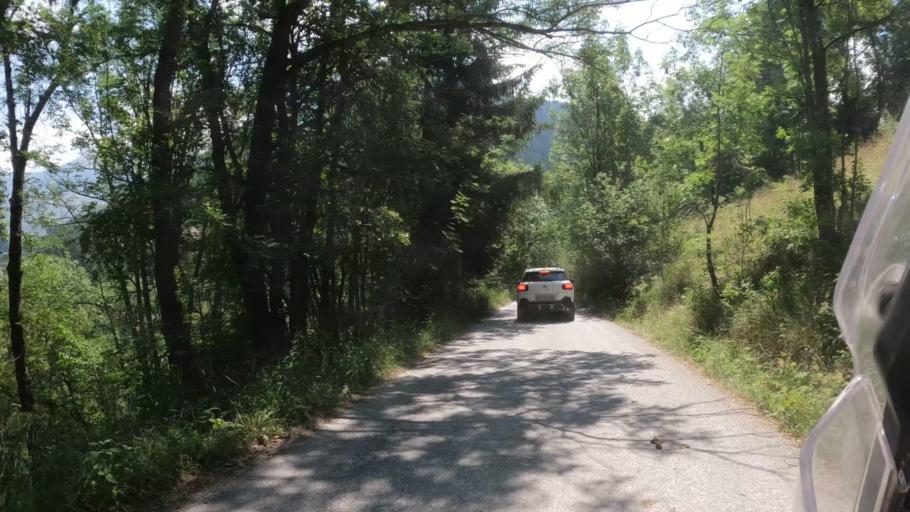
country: IT
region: Piedmont
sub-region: Provincia di Torino
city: Cesana Torinese
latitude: 44.9315
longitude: 6.8174
